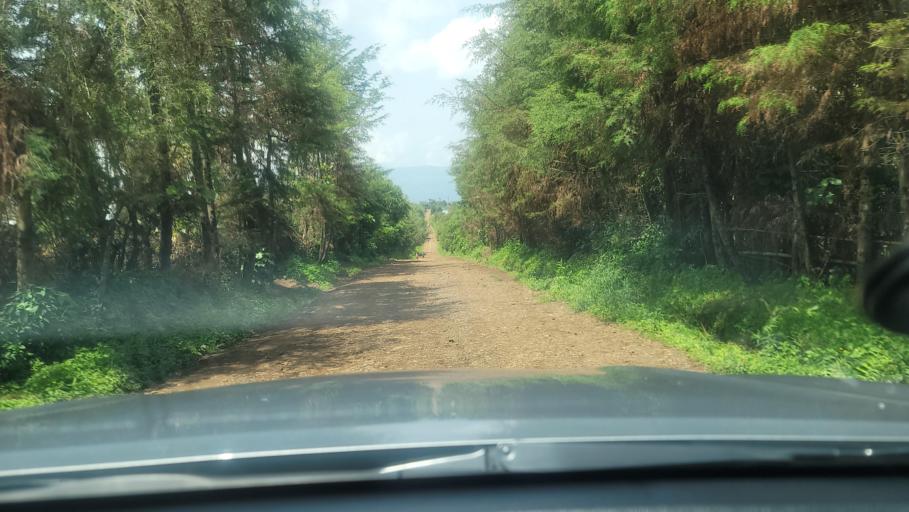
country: ET
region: Oromiya
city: Agaro
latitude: 7.8280
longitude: 36.4074
